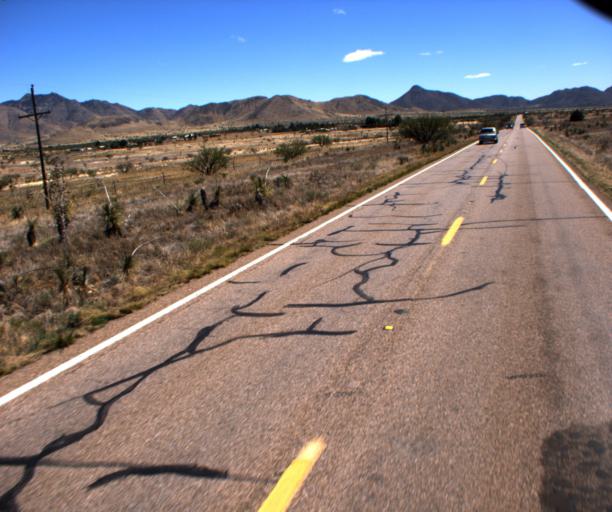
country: US
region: Arizona
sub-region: Cochise County
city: Huachuca City
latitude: 31.7240
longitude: -110.5025
